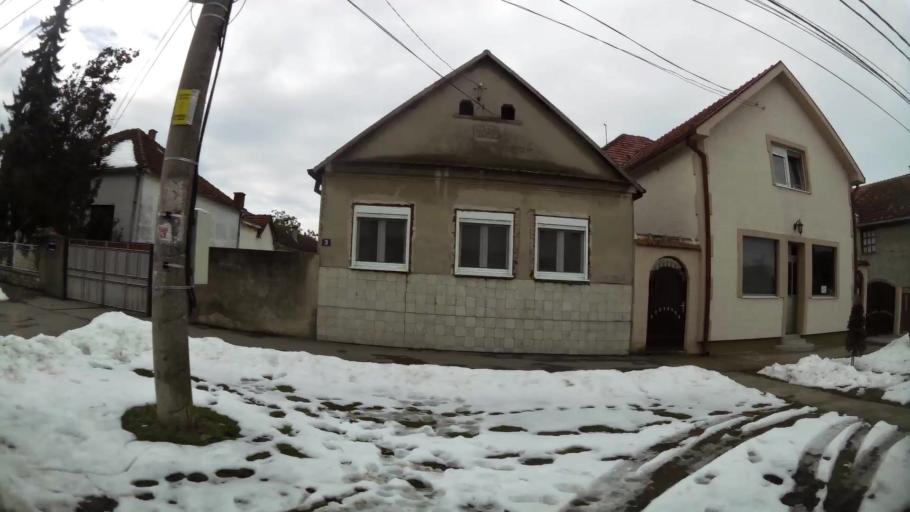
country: RS
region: Central Serbia
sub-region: Belgrade
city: Surcin
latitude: 44.7897
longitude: 20.2615
